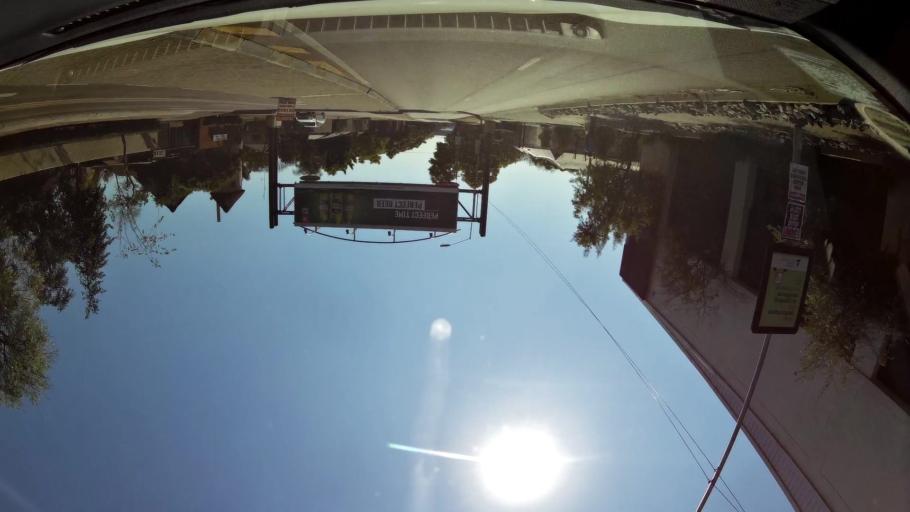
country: ZA
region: Gauteng
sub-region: City of Tshwane Metropolitan Municipality
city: Pretoria
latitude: -25.7665
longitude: 28.2361
